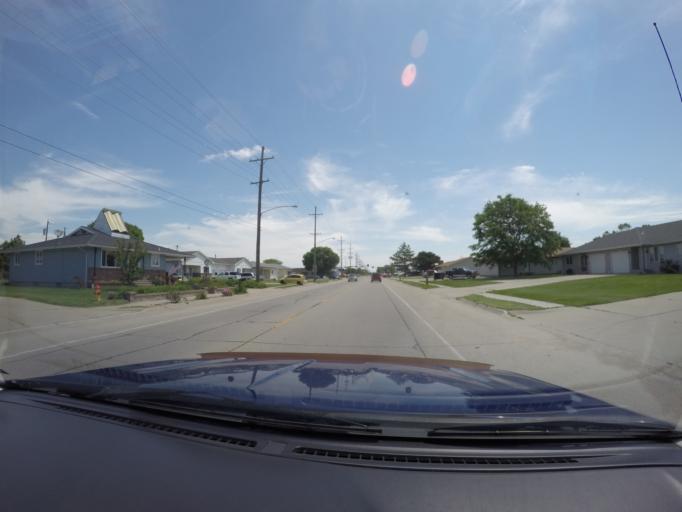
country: US
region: Nebraska
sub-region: Hall County
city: Grand Island
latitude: 40.9021
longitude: -98.3419
